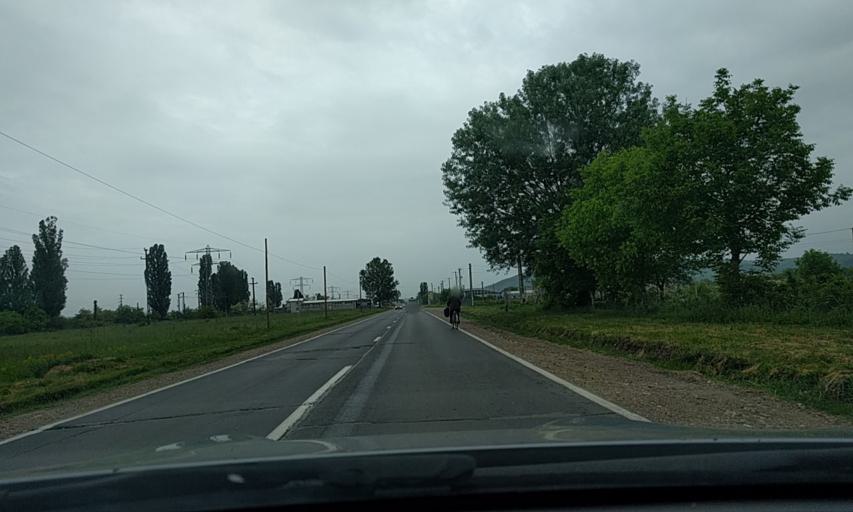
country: RO
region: Dambovita
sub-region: Comuna Aninoasa
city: Aninoasa
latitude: 44.9594
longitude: 25.4431
